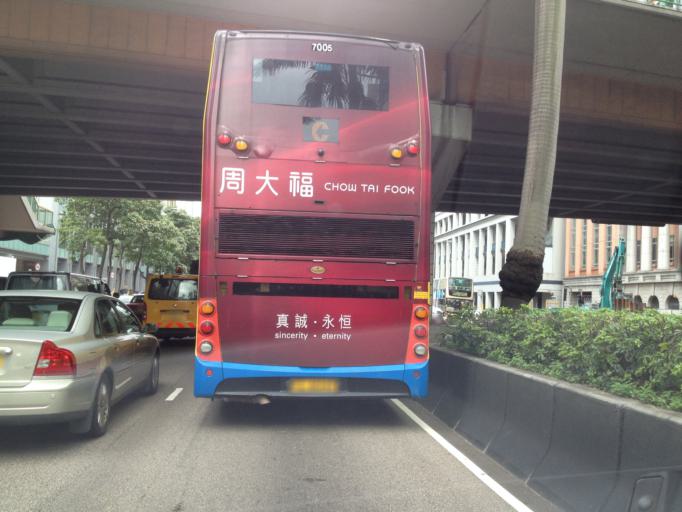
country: HK
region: Wanchai
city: Wan Chai
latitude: 22.2794
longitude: 114.1743
